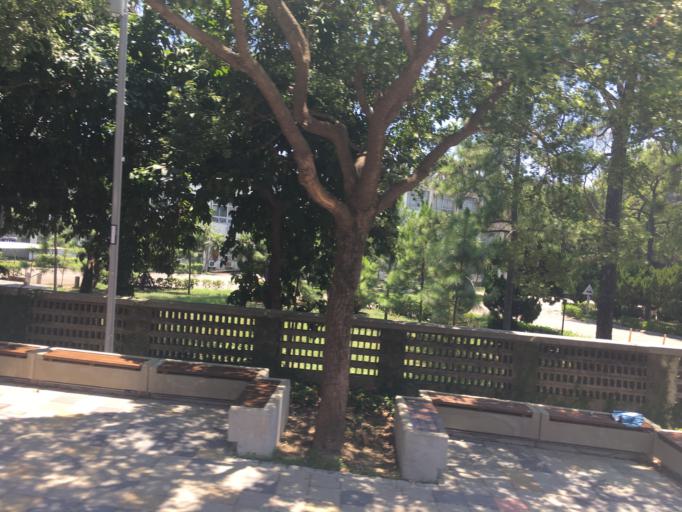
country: TW
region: Taiwan
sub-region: Hsinchu
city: Hsinchu
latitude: 24.7984
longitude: 120.9835
